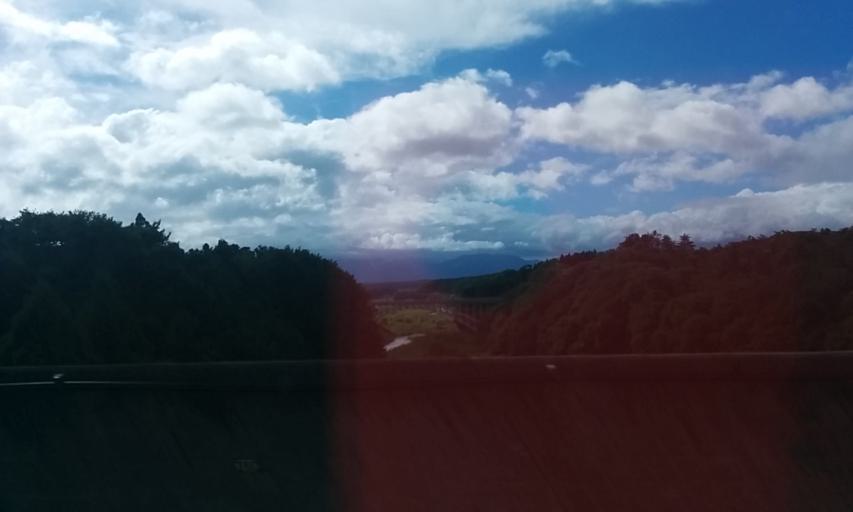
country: JP
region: Tochigi
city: Kuroiso
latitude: 36.9769
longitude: 140.0656
